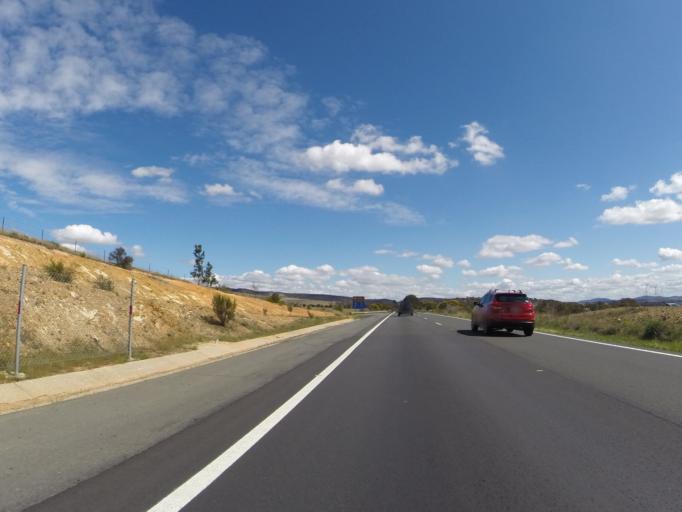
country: AU
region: New South Wales
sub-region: Goulburn Mulwaree
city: Goulburn
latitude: -34.7345
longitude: 149.7976
